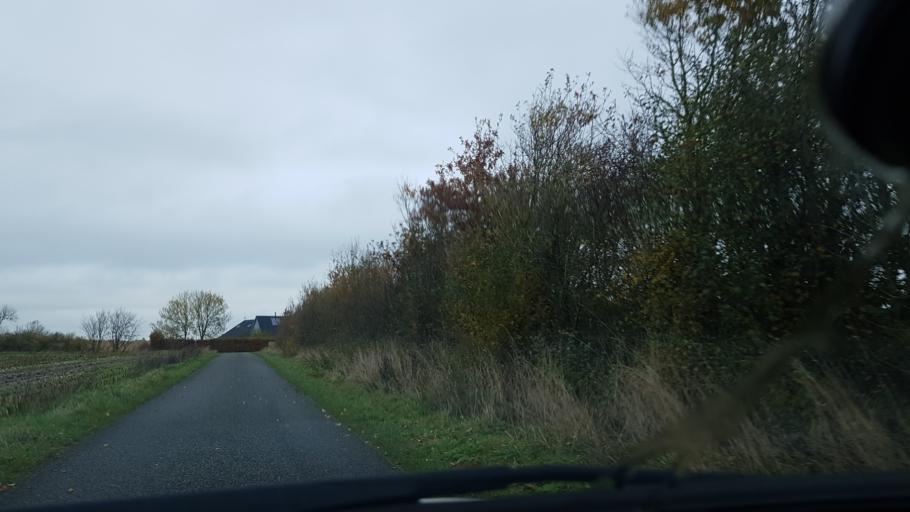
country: DK
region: South Denmark
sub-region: Esbjerg Kommune
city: Ribe
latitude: 55.2597
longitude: 8.8376
